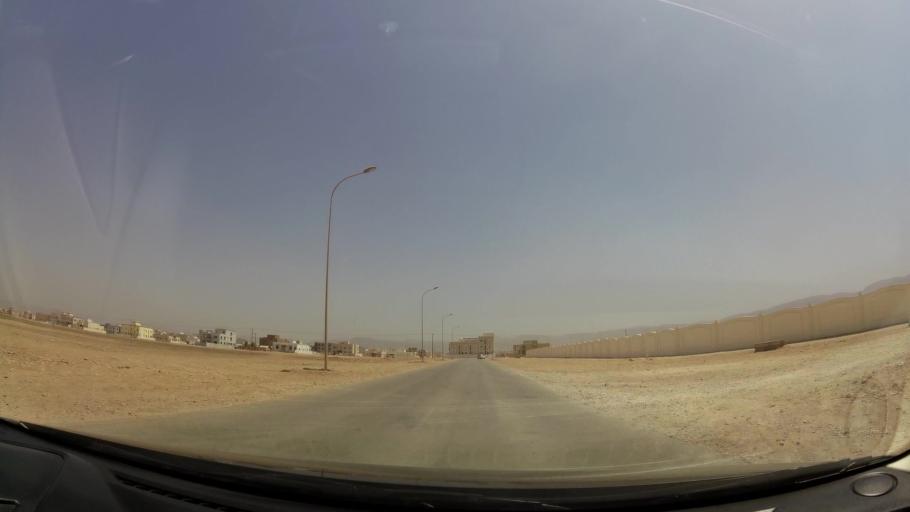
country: OM
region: Zufar
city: Salalah
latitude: 17.0668
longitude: 54.2105
